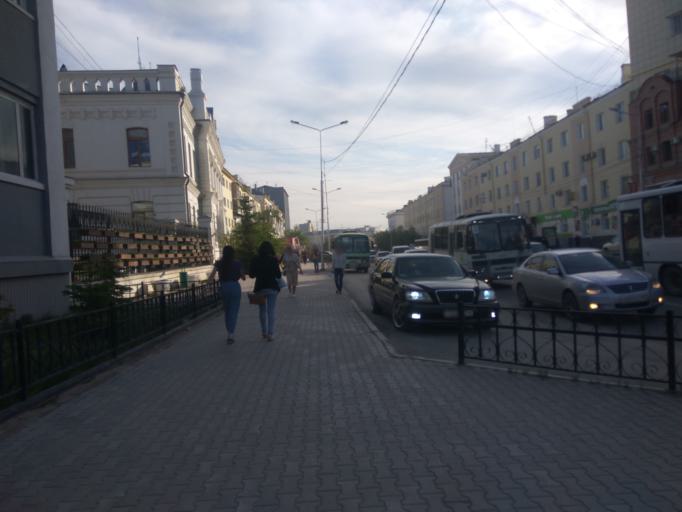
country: RU
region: Sakha
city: Yakutsk
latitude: 62.0249
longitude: 129.7254
